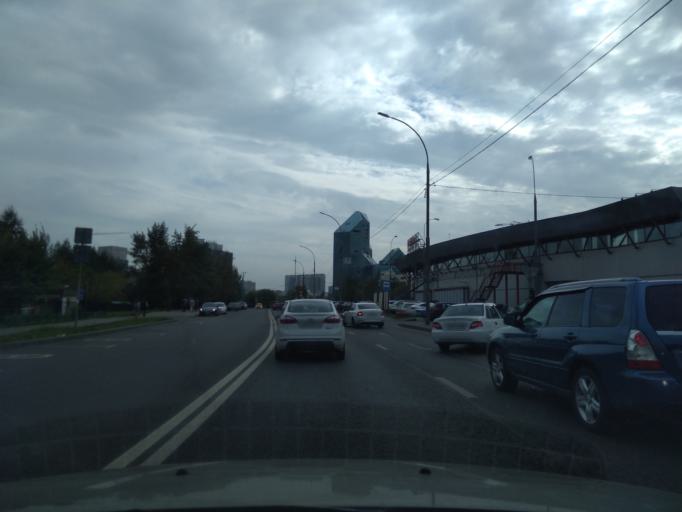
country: RU
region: Moscow
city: Nikulino
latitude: 55.6713
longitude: 37.4771
